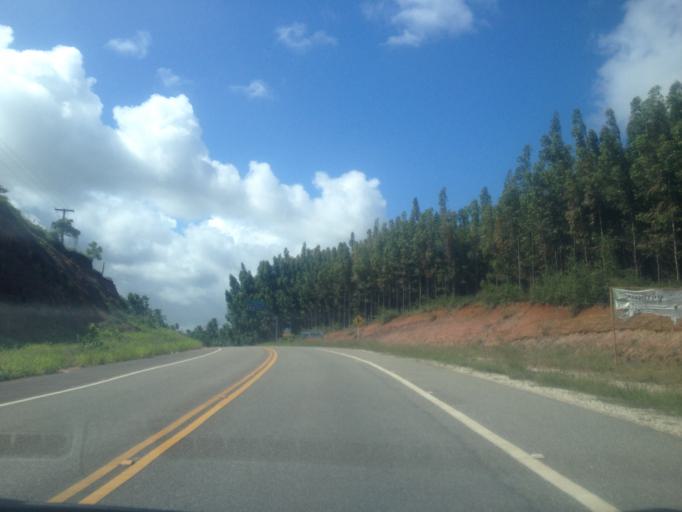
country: BR
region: Sergipe
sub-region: Indiaroba
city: Indiaroba
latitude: -11.4855
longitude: -37.4705
